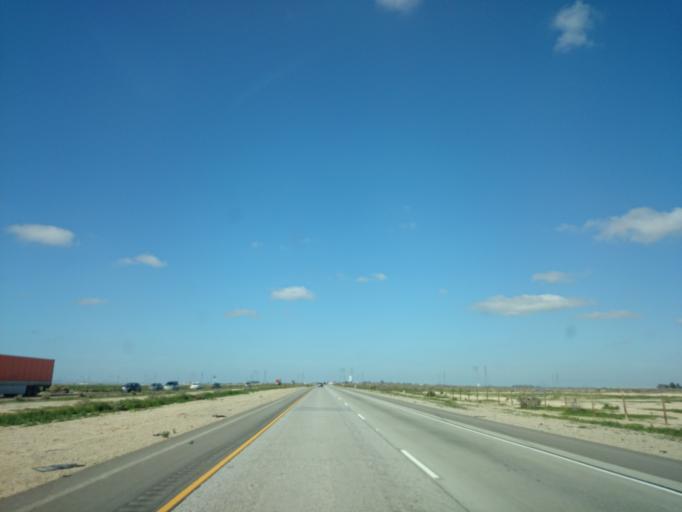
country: US
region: California
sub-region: Kern County
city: Buttonwillow
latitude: 35.3772
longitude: -119.3671
